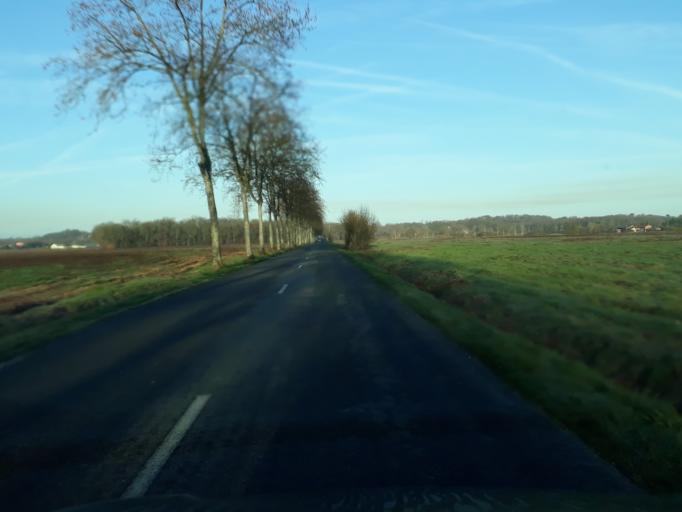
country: FR
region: Midi-Pyrenees
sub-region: Departement de la Haute-Garonne
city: Rieumes
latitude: 43.4246
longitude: 1.1439
